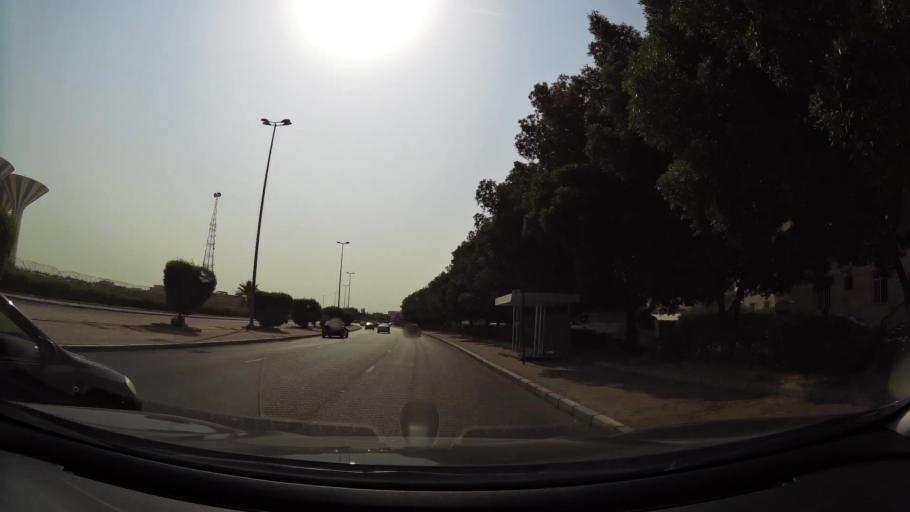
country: KW
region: Al Asimah
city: Ar Rabiyah
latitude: 29.2897
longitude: 47.8795
